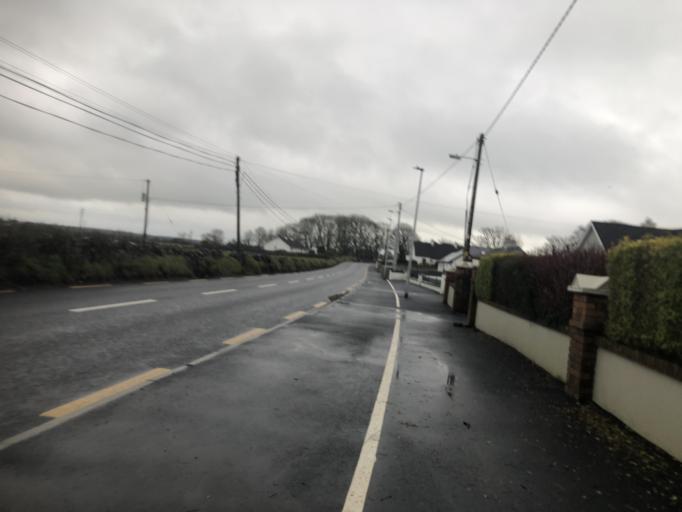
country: IE
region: Connaught
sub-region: County Galway
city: Tuam
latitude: 53.5055
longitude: -8.8273
